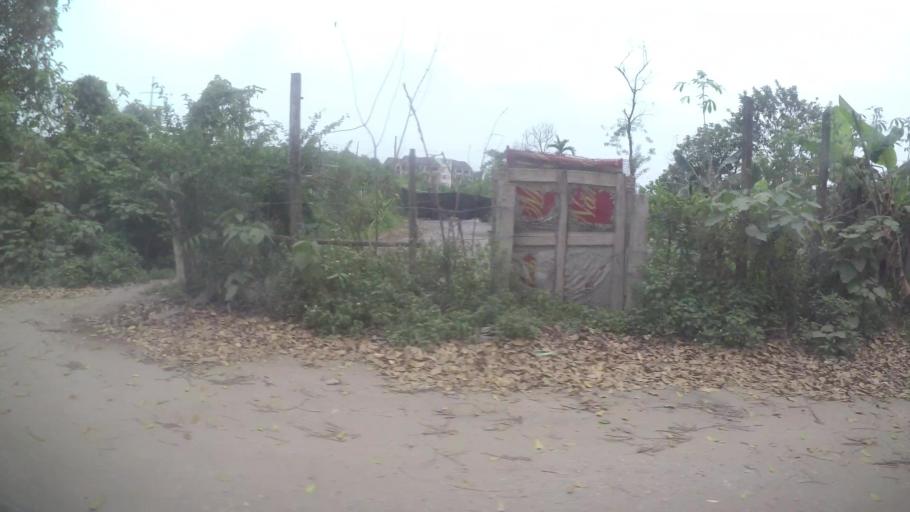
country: VN
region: Ha Noi
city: Cau Dien
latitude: 21.0238
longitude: 105.7425
